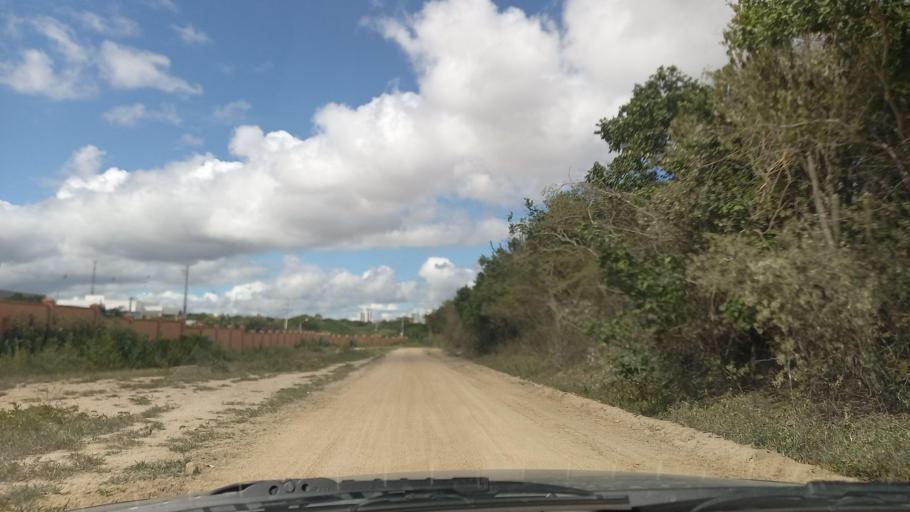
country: BR
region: Pernambuco
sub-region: Caruaru
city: Caruaru
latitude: -8.2481
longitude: -35.9820
